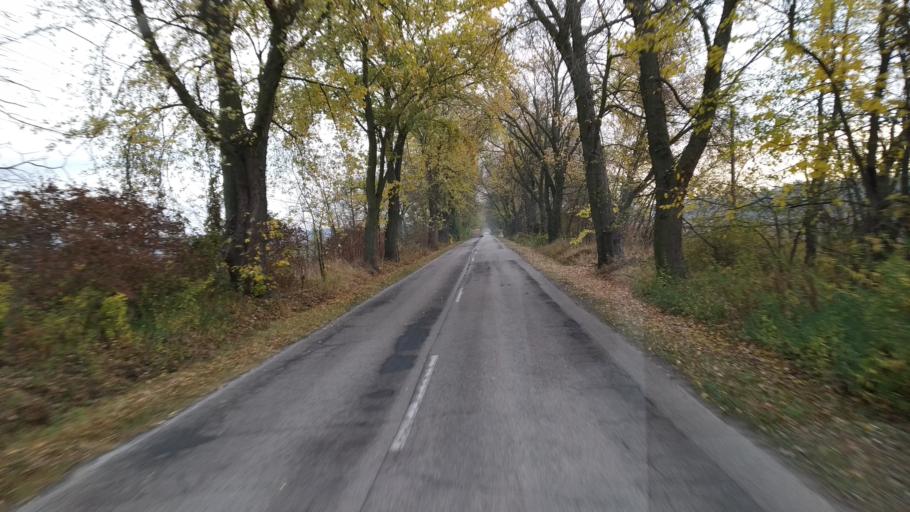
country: HU
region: Pest
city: Dunabogdany
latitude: 47.7991
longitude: 19.0483
